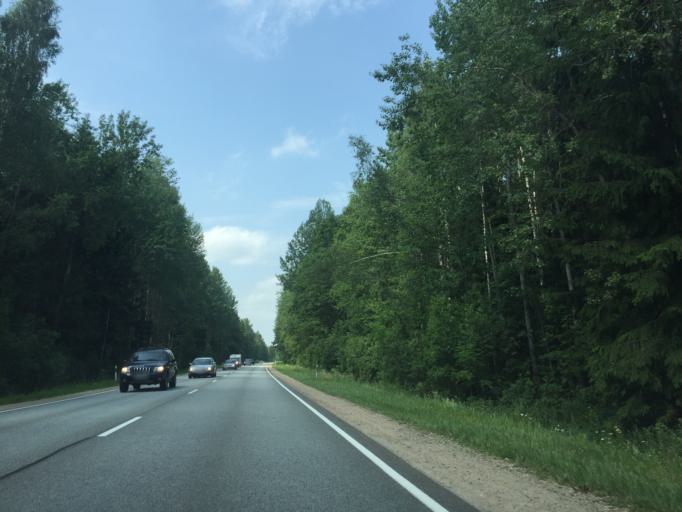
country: LV
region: Kekava
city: Balozi
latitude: 56.8221
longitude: 24.0825
